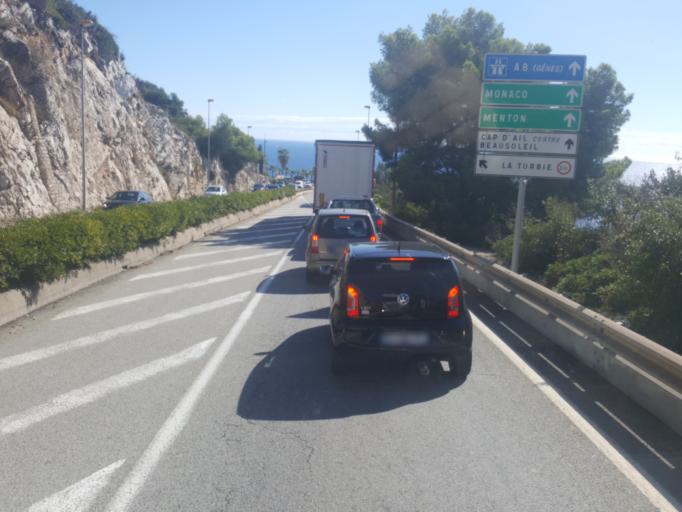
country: FR
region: Provence-Alpes-Cote d'Azur
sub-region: Departement des Alpes-Maritimes
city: Cap-d'Ail
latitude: 43.7252
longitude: 7.3900
